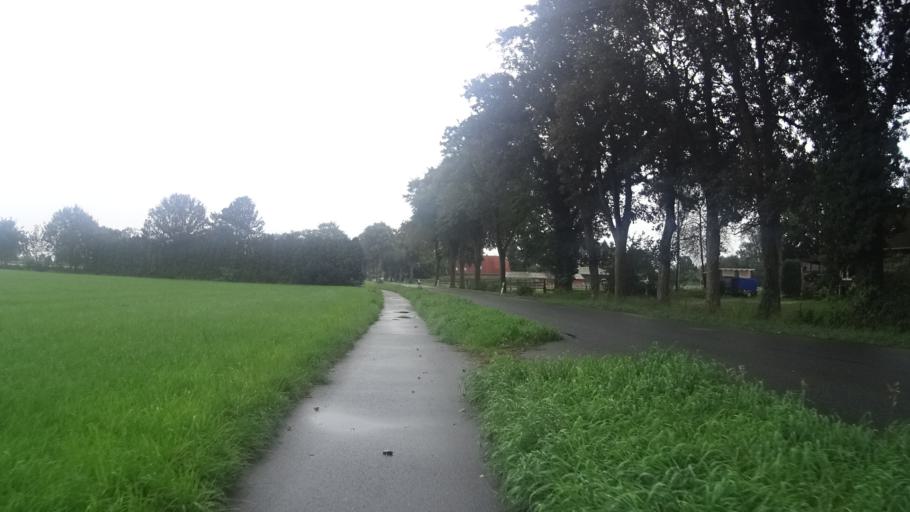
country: DE
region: Schleswig-Holstein
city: Seeth-Ekholt
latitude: 53.7572
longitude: 9.7329
